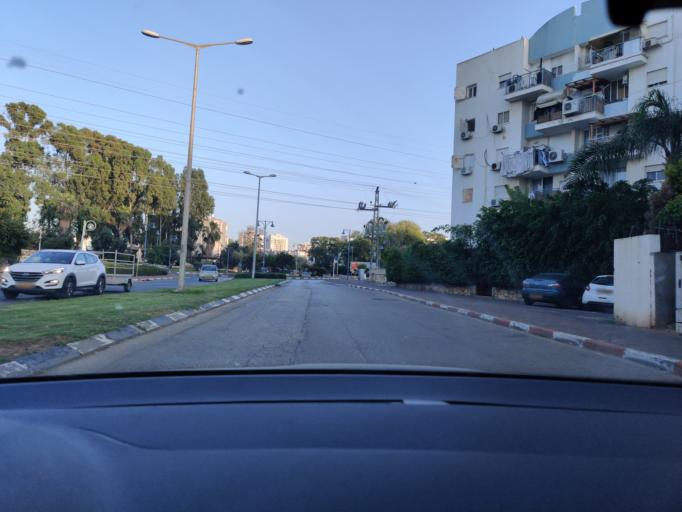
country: IL
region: Haifa
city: Hadera
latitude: 32.4740
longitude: 34.9518
